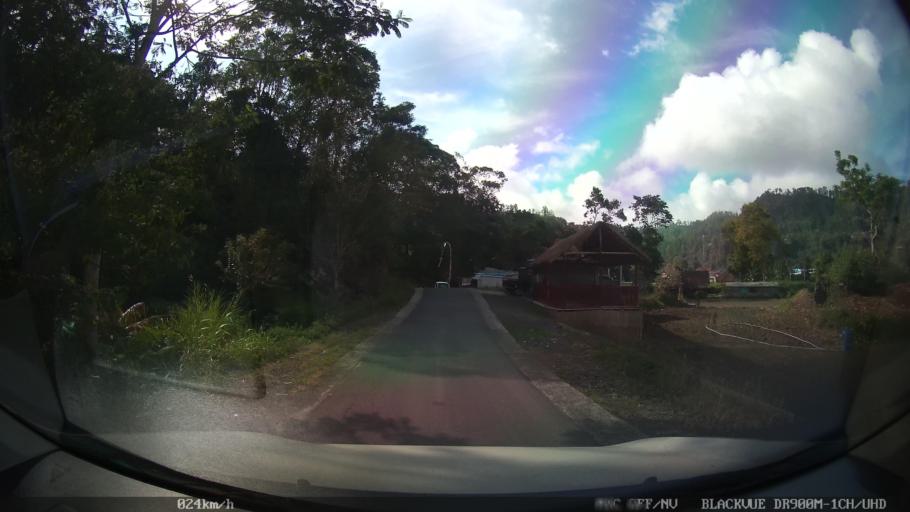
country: ID
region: Bali
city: Banjar Trunyan
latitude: -8.2257
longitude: 115.4112
